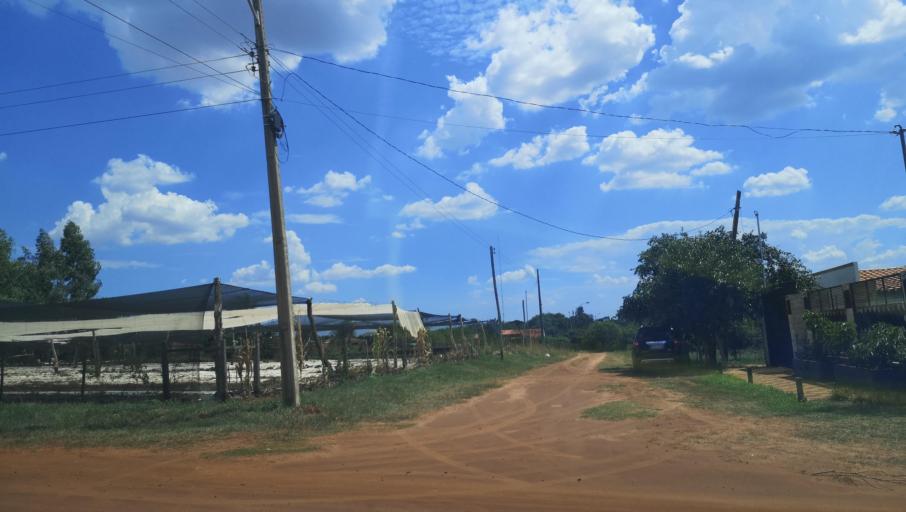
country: PY
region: Misiones
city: Santa Maria
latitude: -26.8914
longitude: -57.0382
